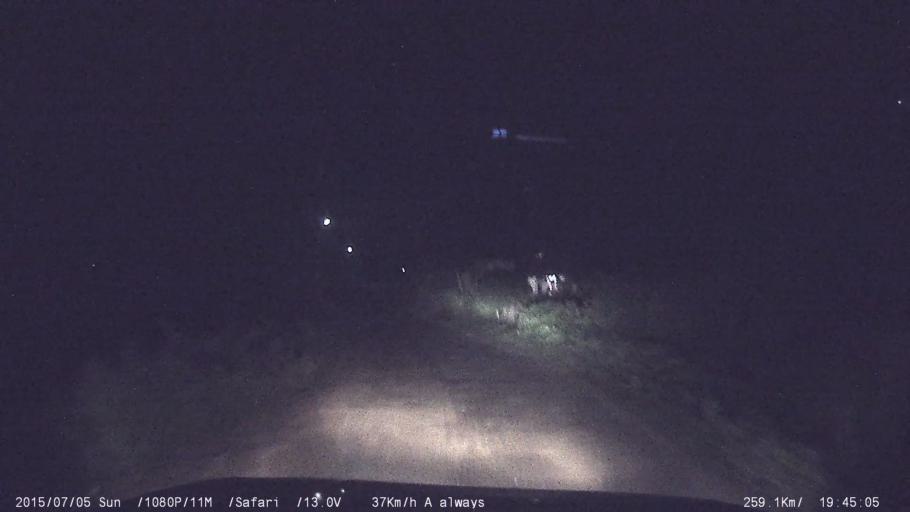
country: IN
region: Kerala
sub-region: Palakkad district
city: Palakkad
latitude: 10.7724
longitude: 76.5517
